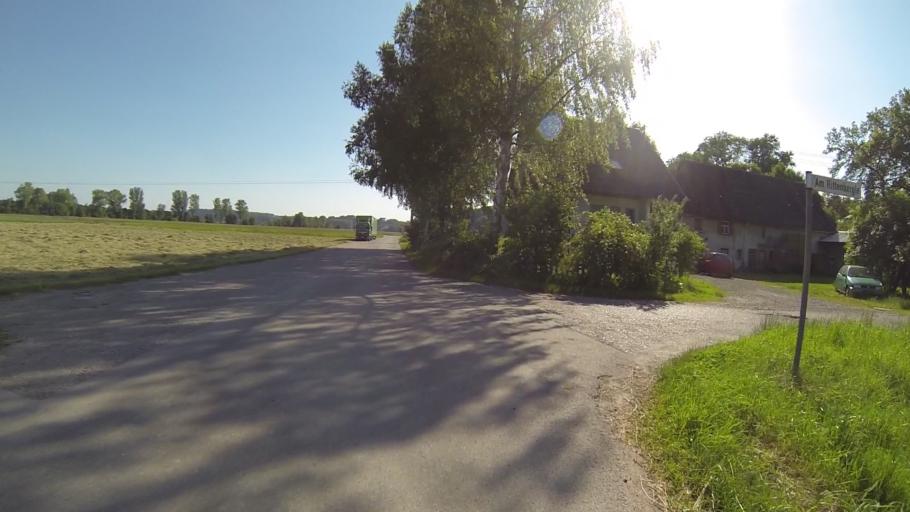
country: DE
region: Baden-Wuerttemberg
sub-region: Tuebingen Region
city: Warthausen
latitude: 48.1701
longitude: 9.8066
